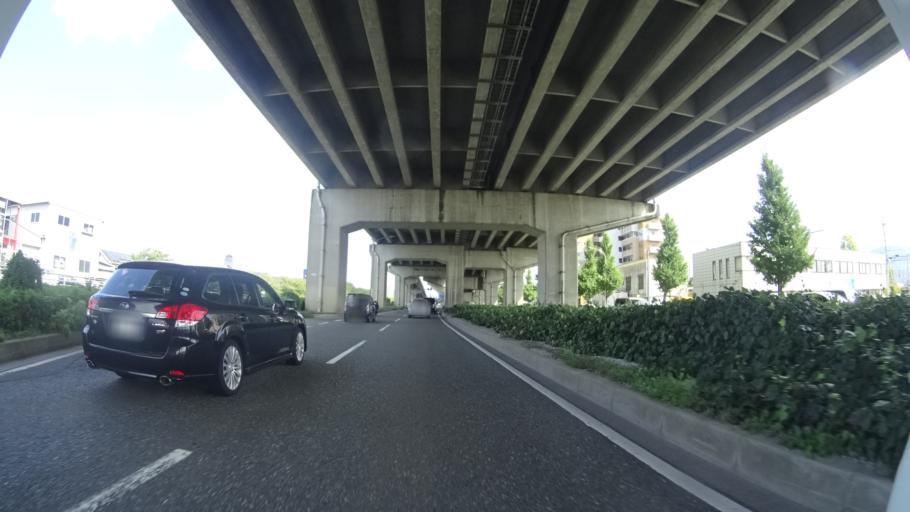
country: JP
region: Fukuoka
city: Kitakyushu
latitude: 33.8398
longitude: 130.8978
